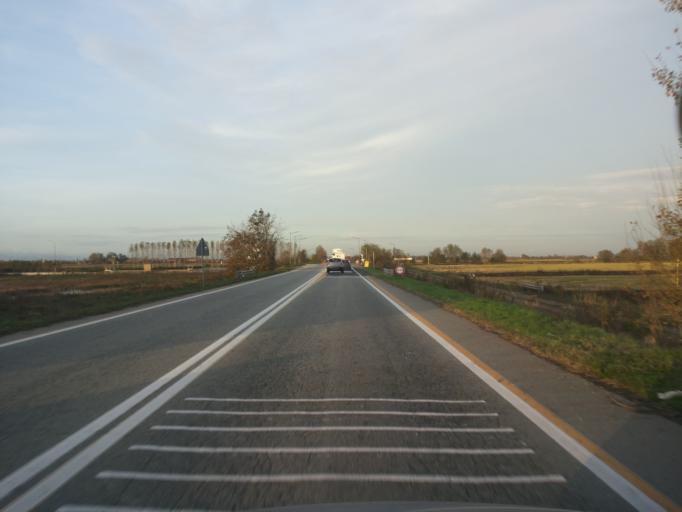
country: IT
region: Piedmont
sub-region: Provincia di Vercelli
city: Tricerro
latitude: 45.2384
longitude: 8.3346
